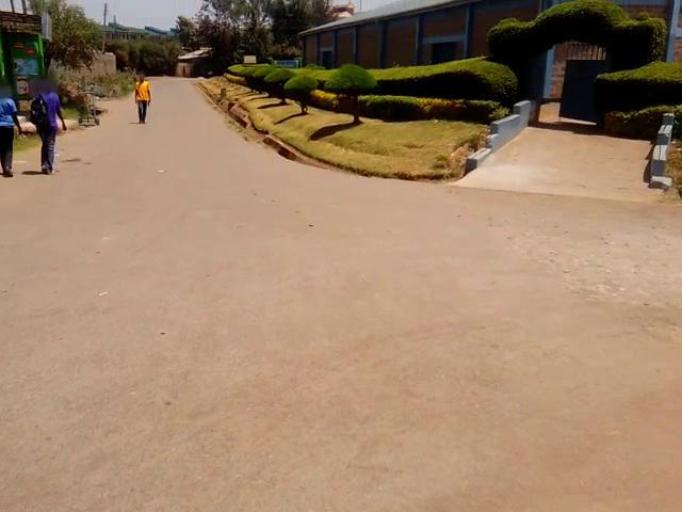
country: KE
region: Nairobi Area
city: Nairobi
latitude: -1.3122
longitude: 36.7759
